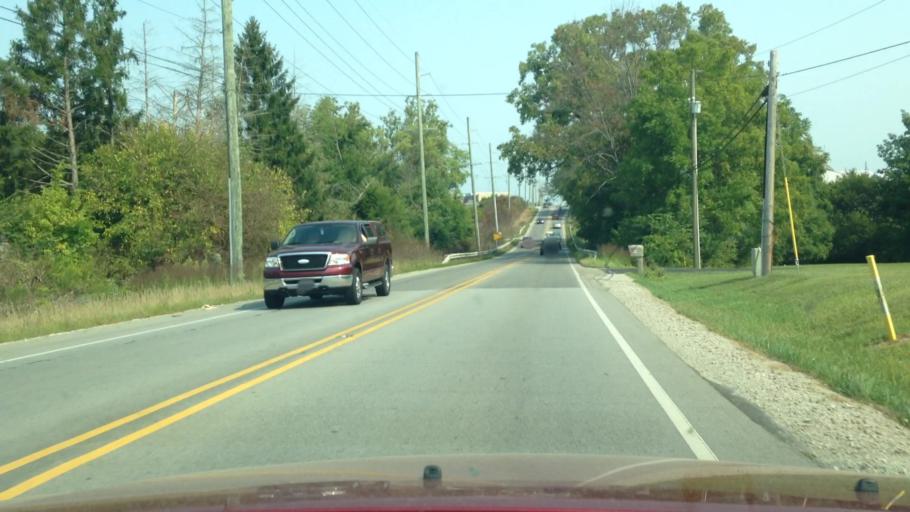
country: US
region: Indiana
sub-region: Johnson County
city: Waterloo
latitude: 39.5662
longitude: -86.1588
